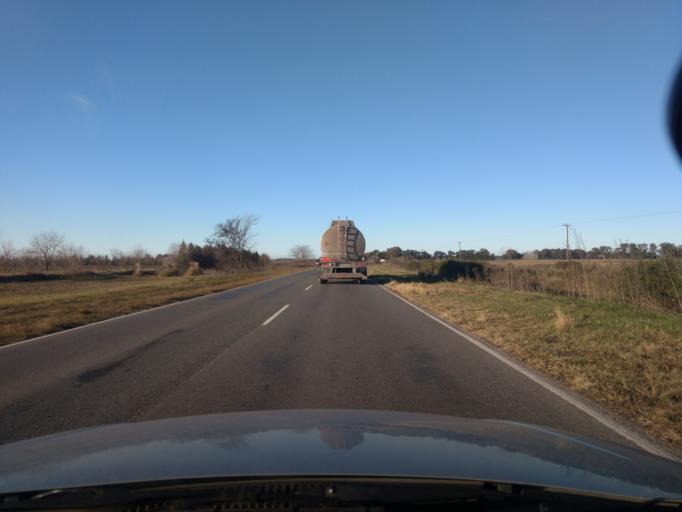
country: AR
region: Buenos Aires
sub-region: Partido de Lujan
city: Lujan
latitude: -34.6426
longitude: -59.1057
